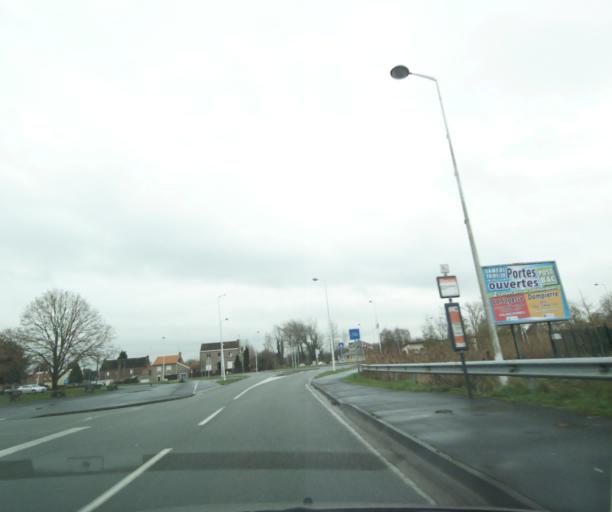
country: FR
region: Nord-Pas-de-Calais
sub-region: Departement du Nord
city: Haulchin
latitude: 50.3257
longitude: 3.4366
